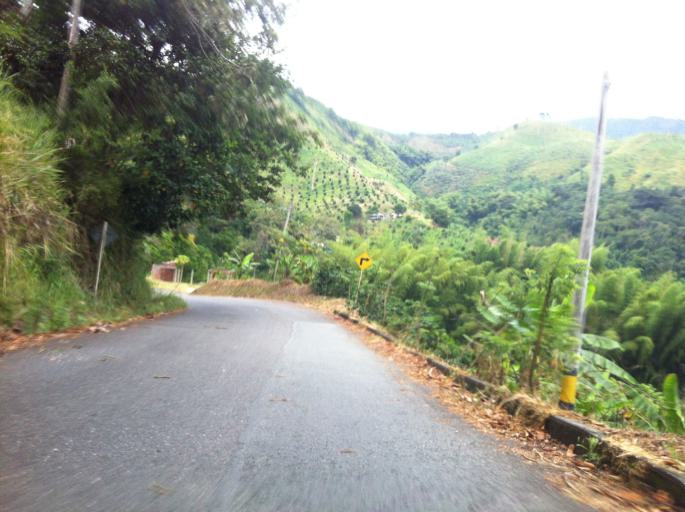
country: CO
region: Quindio
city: Buenavista
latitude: 4.3677
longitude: -75.7579
